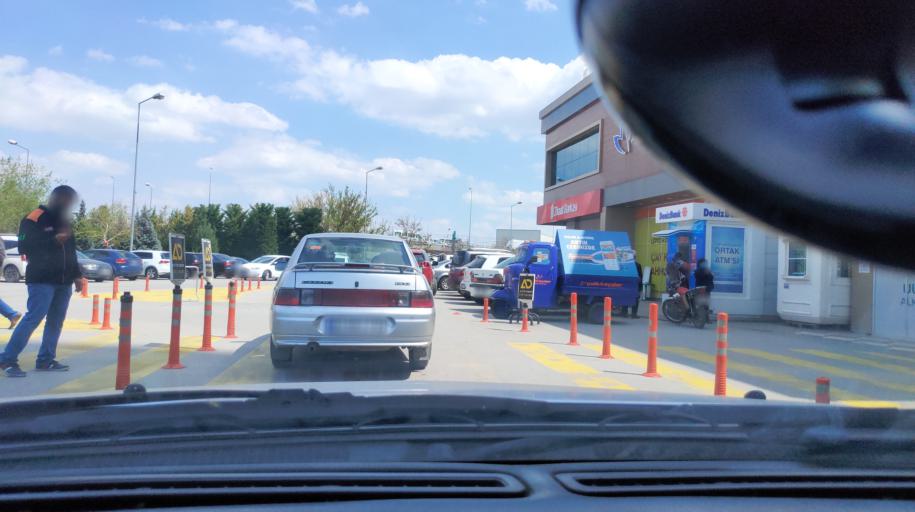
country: TR
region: Konya
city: Selcuklu
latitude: 37.9281
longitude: 32.5077
